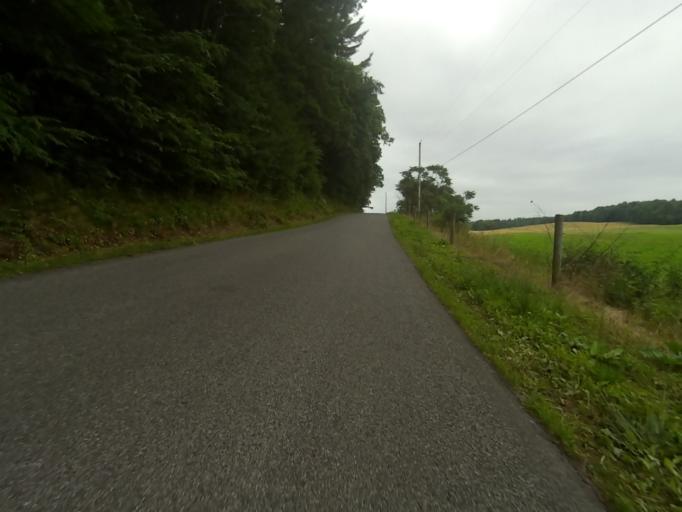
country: US
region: Pennsylvania
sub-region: Centre County
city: Stormstown
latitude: 40.6948
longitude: -78.0964
